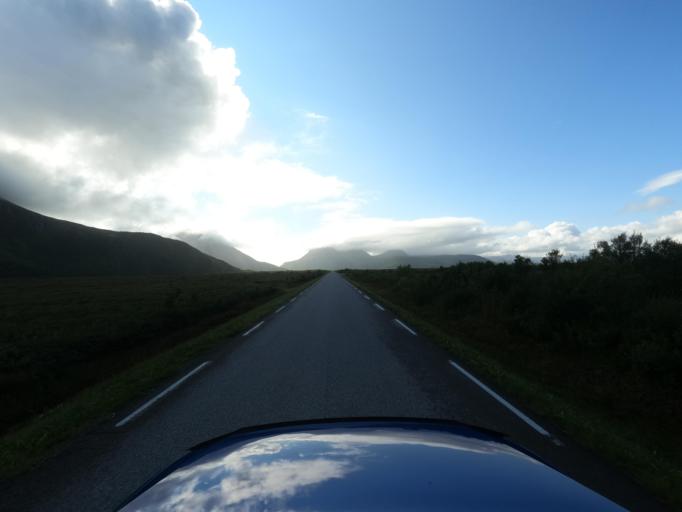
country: NO
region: Nordland
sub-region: Vagan
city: Kabelvag
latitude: 68.3059
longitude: 14.1790
